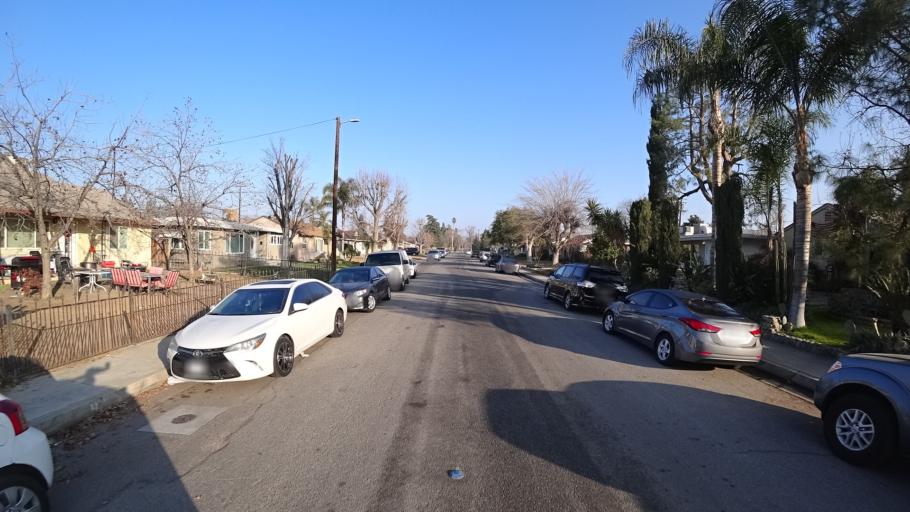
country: US
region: California
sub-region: Kern County
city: Bakersfield
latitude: 35.3597
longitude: -119.0414
